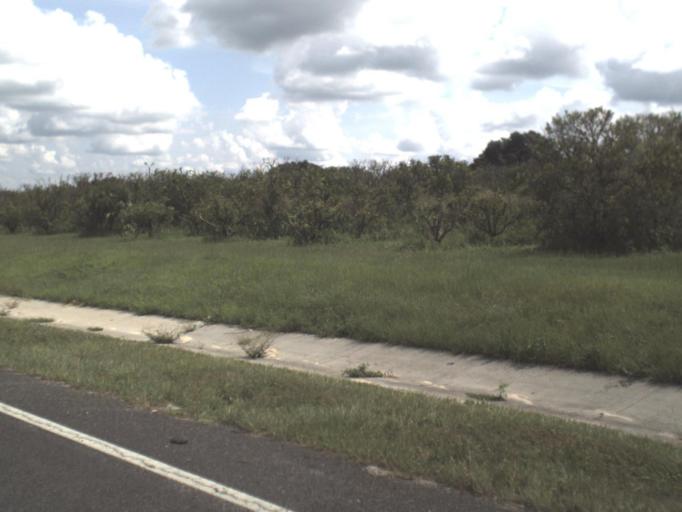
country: US
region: Florida
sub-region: Pasco County
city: Dade City
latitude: 28.3307
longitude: -82.1874
